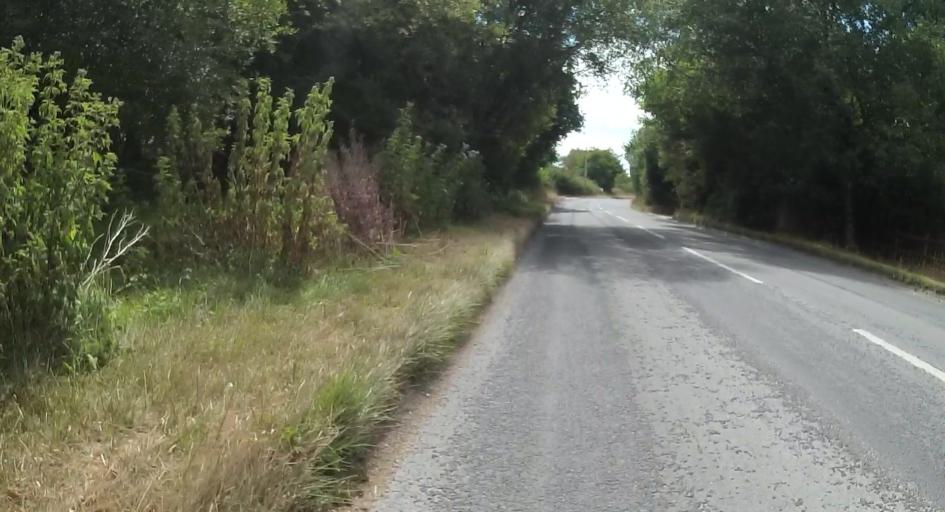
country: GB
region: England
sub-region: Dorset
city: Wareham
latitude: 50.6635
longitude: -2.1014
